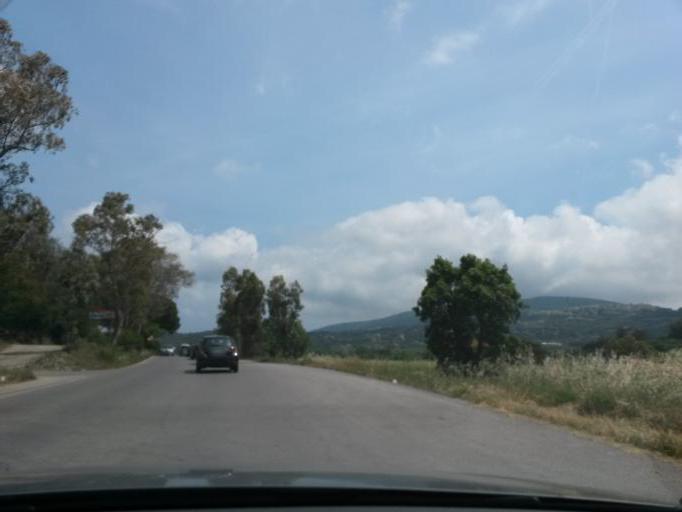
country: IT
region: Tuscany
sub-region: Provincia di Livorno
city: Capoliveri
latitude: 42.7614
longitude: 10.3646
